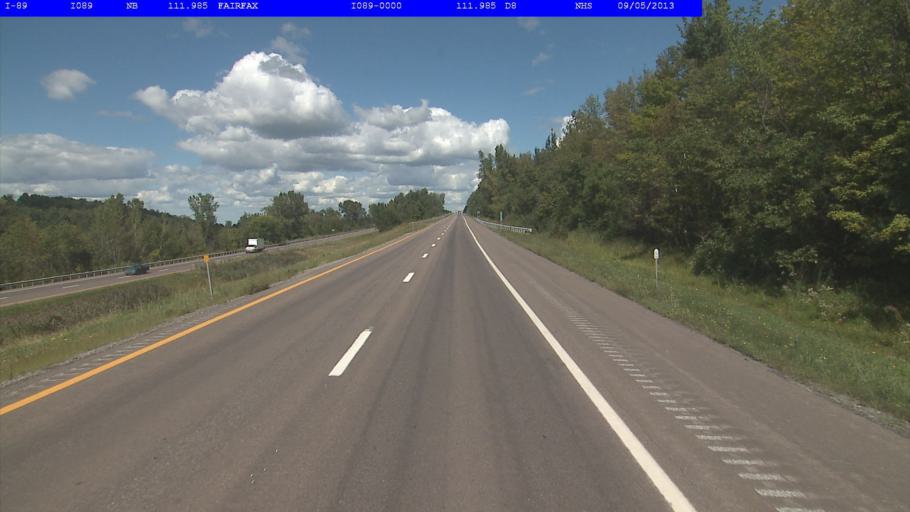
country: US
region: Vermont
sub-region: Franklin County
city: Saint Albans
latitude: 44.7697
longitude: -73.0753
